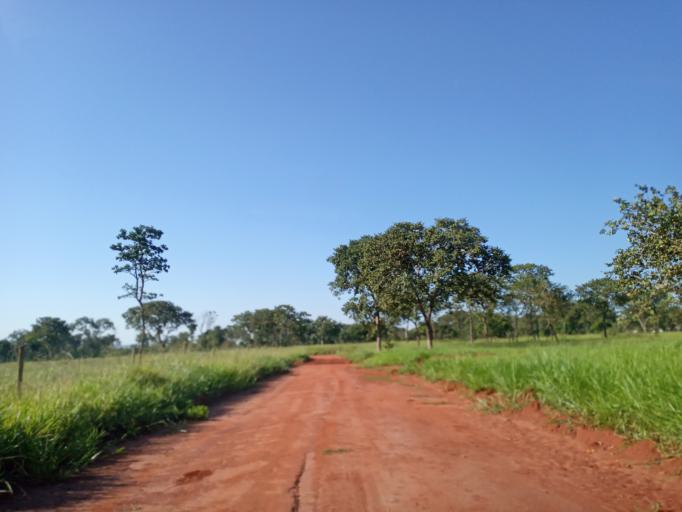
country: BR
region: Minas Gerais
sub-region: Ituiutaba
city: Ituiutaba
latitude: -18.9677
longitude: -49.4995
